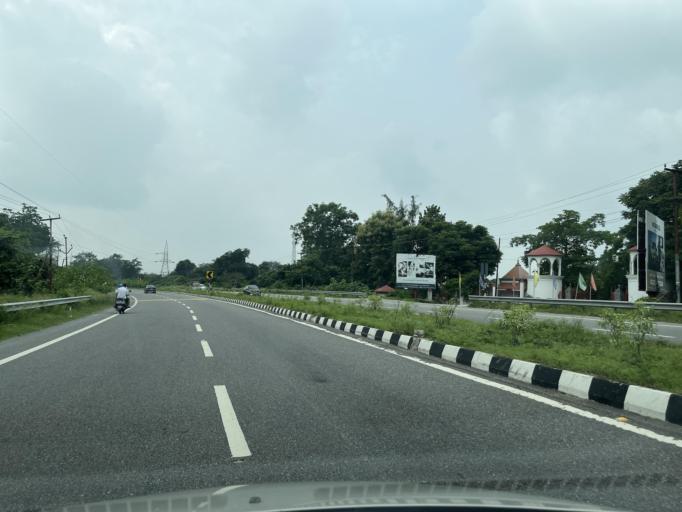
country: IN
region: Uttarakhand
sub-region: Dehradun
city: Doiwala
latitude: 30.1154
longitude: 78.1677
